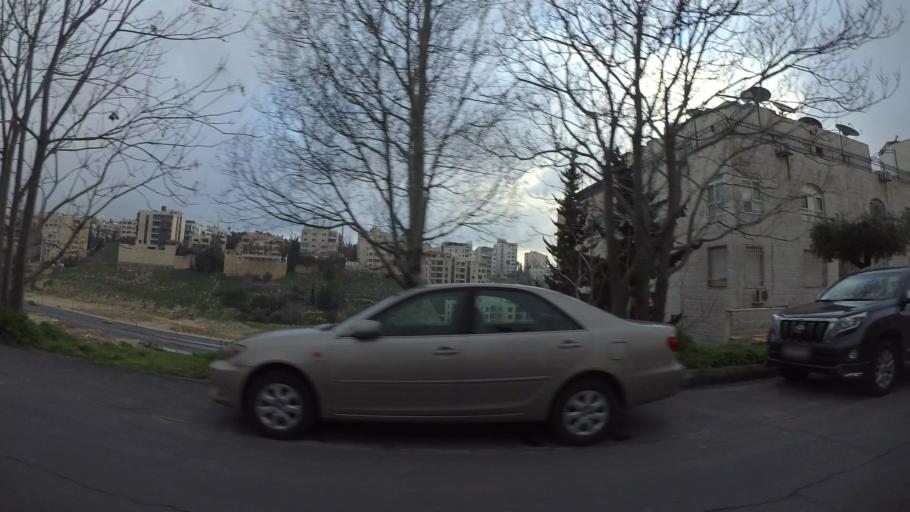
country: JO
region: Amman
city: Amman
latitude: 31.9509
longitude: 35.8924
